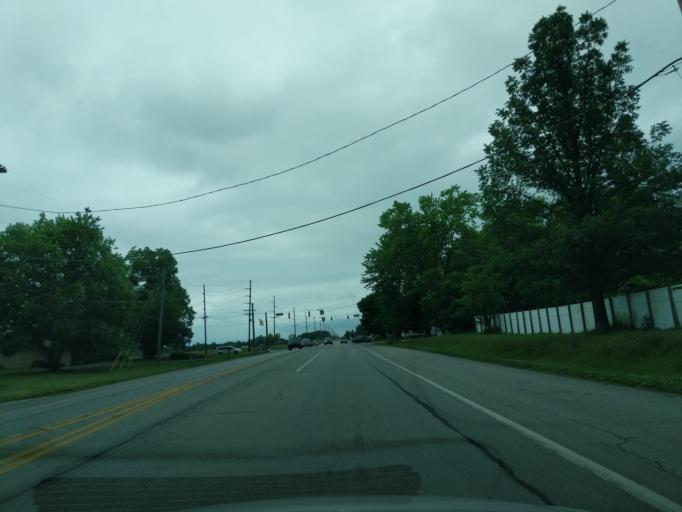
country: US
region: Indiana
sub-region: Hamilton County
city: Cicero
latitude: 40.0865
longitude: -86.0143
